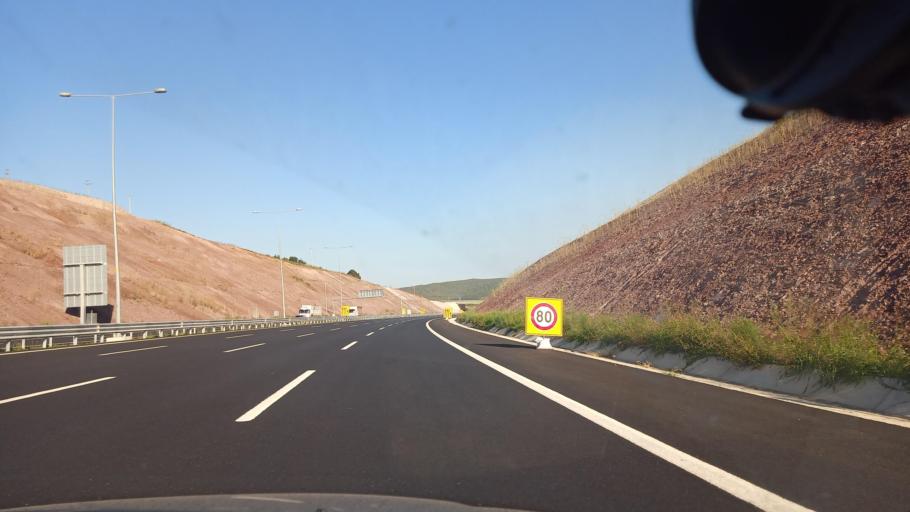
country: TR
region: Sakarya
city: Adapazari
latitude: 40.8392
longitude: 30.3764
